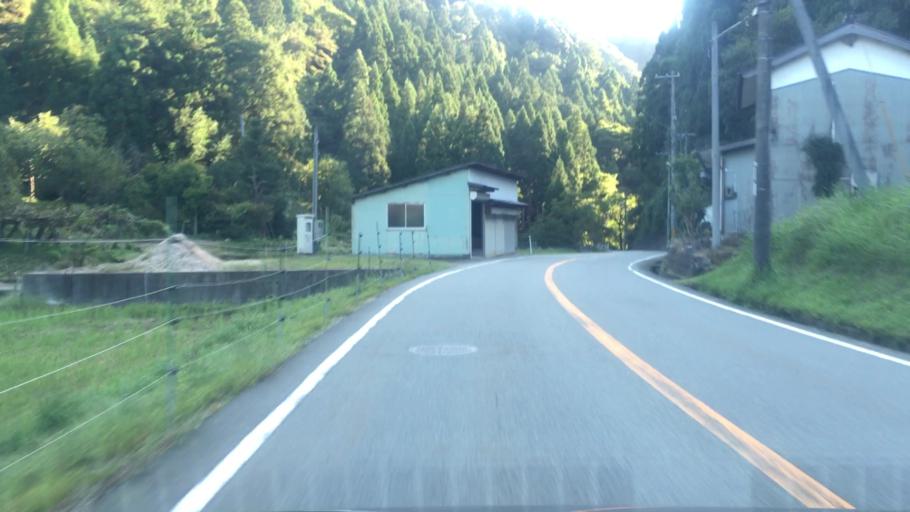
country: JP
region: Hyogo
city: Toyooka
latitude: 35.6201
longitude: 134.8617
